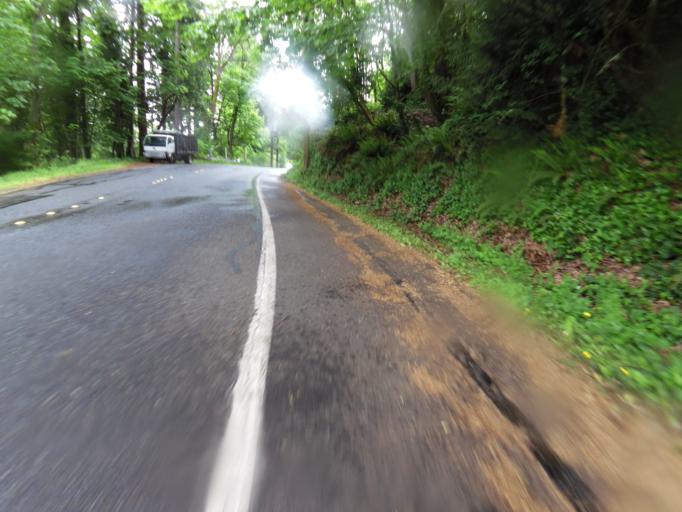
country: US
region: Washington
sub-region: King County
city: Mercer Island
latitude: 47.5507
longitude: -122.2131
